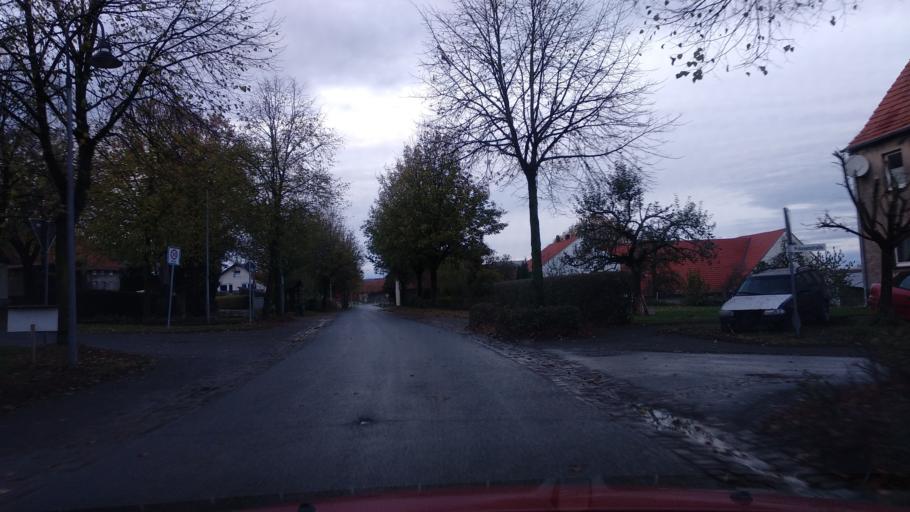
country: DE
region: North Rhine-Westphalia
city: Borgentreich
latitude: 51.6585
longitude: 9.2730
